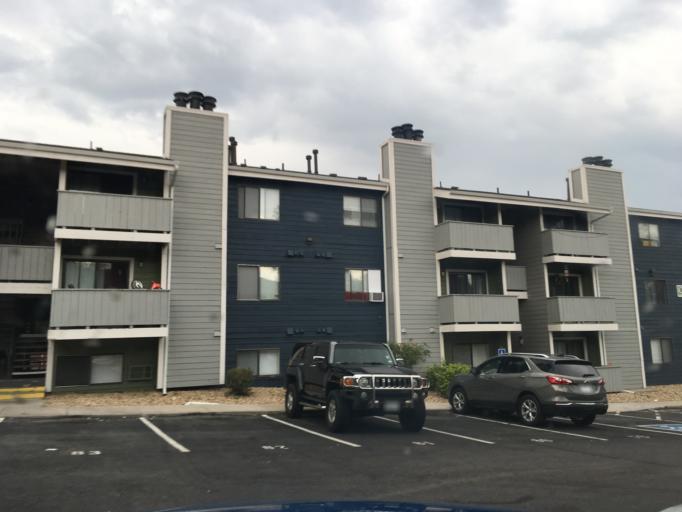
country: US
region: Colorado
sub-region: Arapahoe County
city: Sheridan
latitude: 39.6584
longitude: -105.0293
